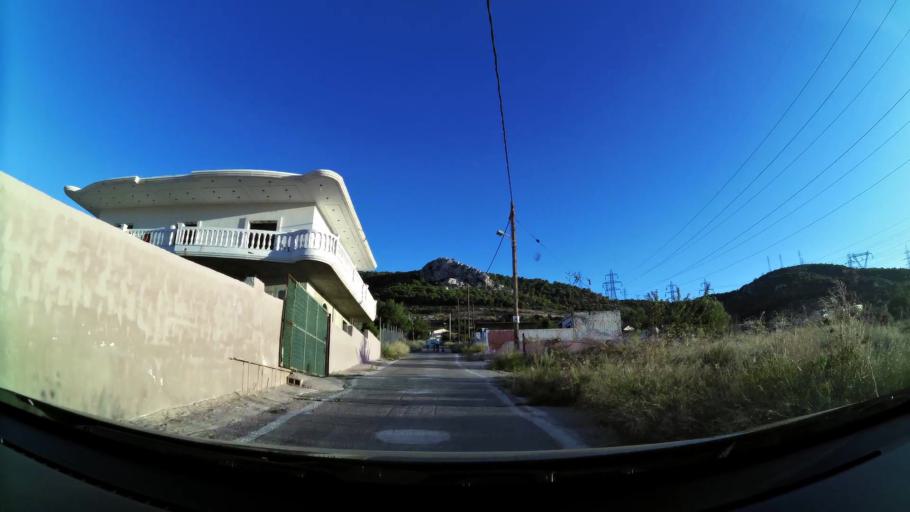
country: GR
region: Attica
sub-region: Nomarchia Athinas
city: Skaramangas
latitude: 38.0306
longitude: 23.6228
